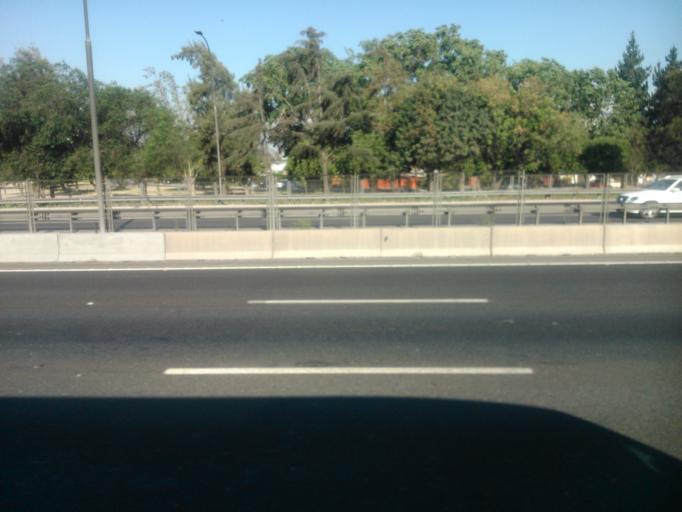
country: CL
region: Santiago Metropolitan
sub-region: Provincia de Maipo
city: San Bernardo
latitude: -33.5887
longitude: -70.7148
